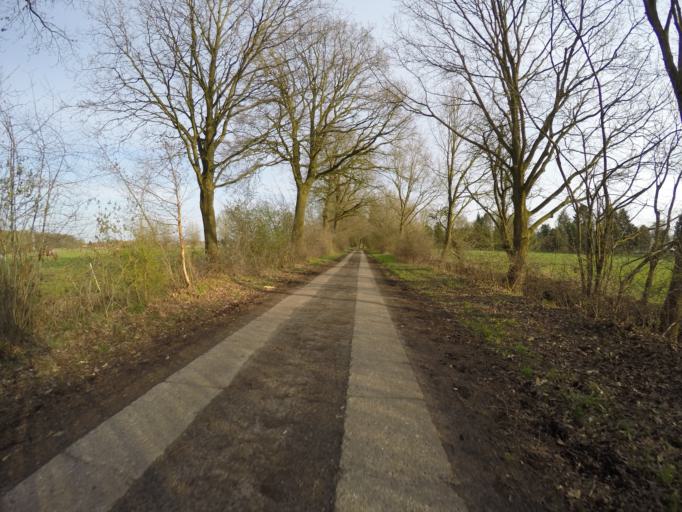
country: DE
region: Schleswig-Holstein
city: Bilsen
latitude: 53.7490
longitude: 9.8718
